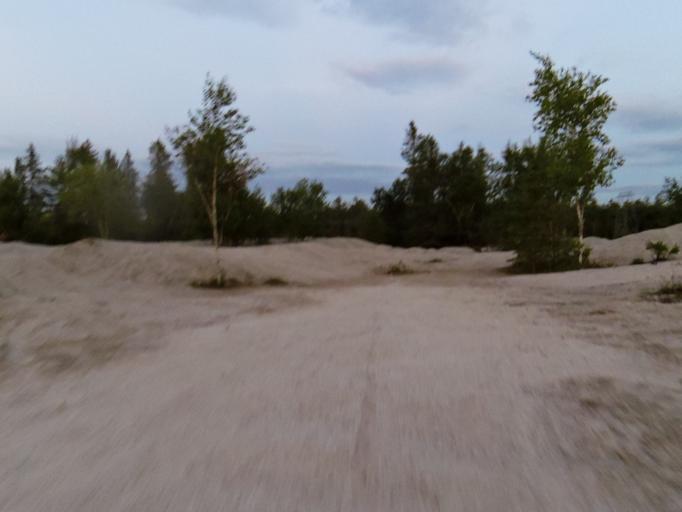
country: CA
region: Ontario
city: Arnprior
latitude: 45.4391
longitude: -76.2560
